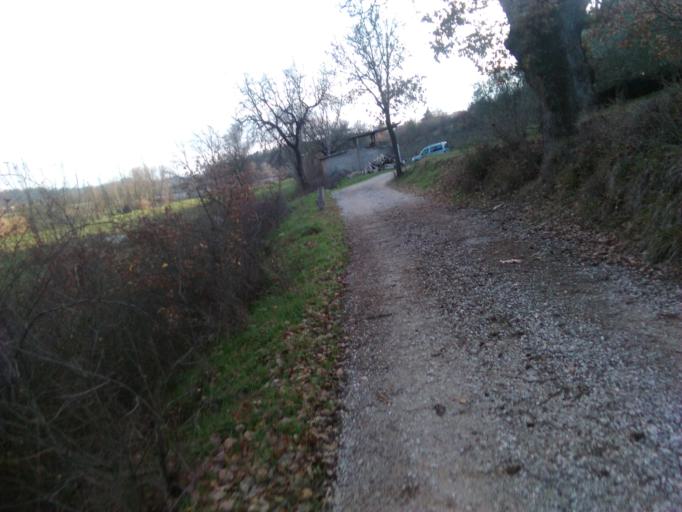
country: IT
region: Umbria
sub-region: Provincia di Perugia
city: Lacugnano
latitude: 43.0895
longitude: 12.3570
